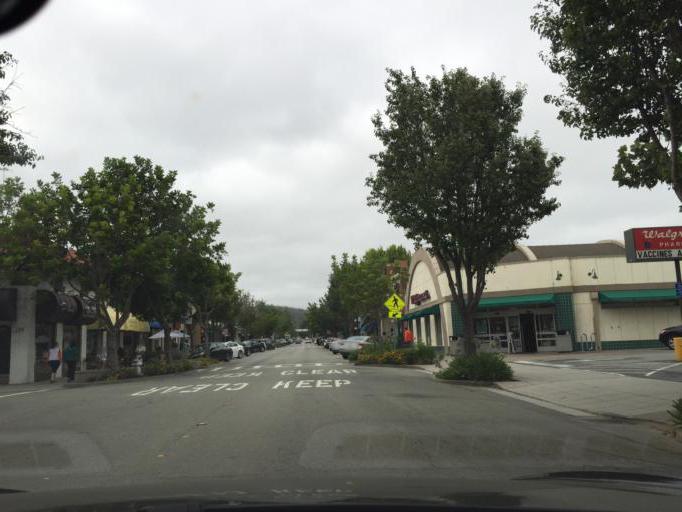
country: US
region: California
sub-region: San Mateo County
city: Burlingame
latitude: 37.5871
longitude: -122.3639
